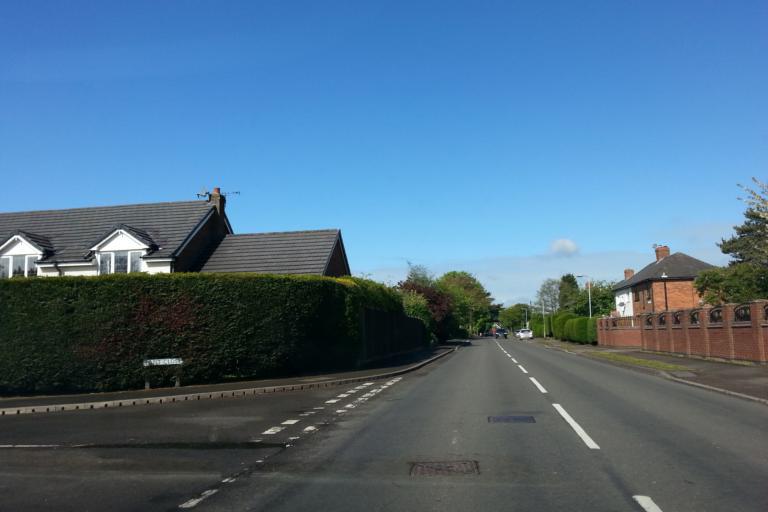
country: GB
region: England
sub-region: Staffordshire
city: Alrewas
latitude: 52.7482
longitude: -1.8114
